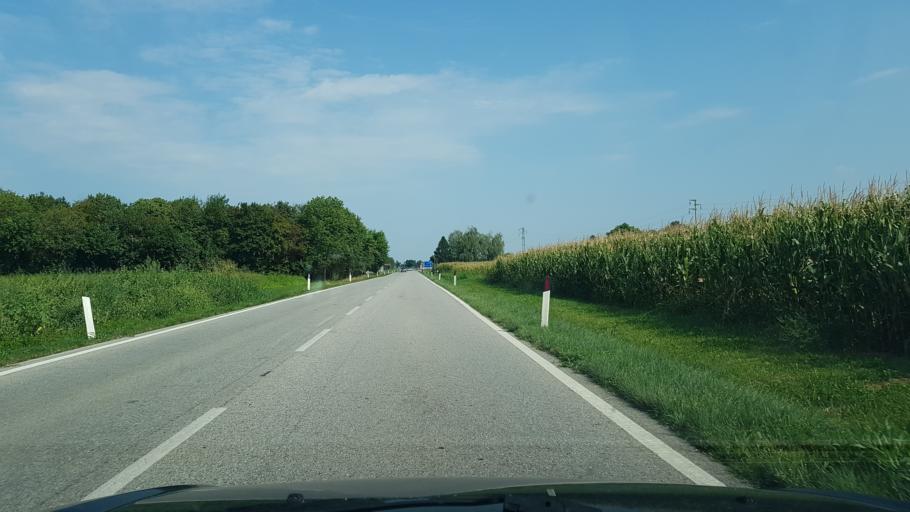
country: IT
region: Friuli Venezia Giulia
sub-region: Provincia di Udine
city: Flaibano
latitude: 46.0845
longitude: 12.9702
